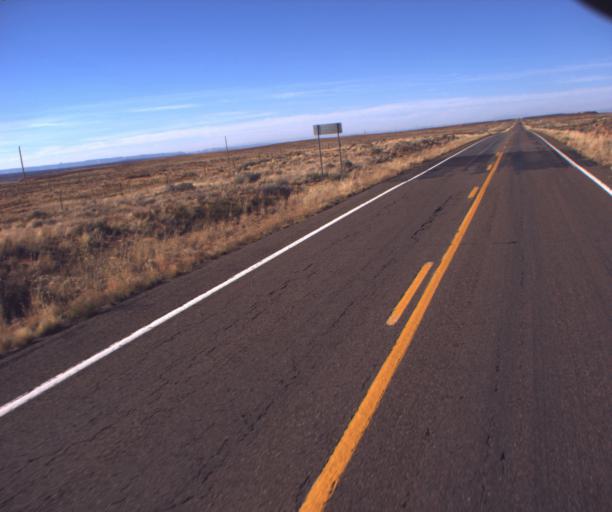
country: US
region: Arizona
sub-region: Coconino County
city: Kaibito
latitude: 36.7055
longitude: -111.2681
